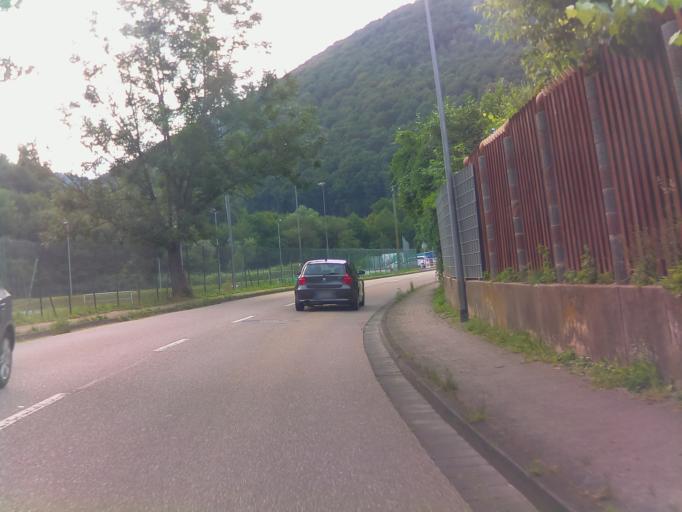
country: DE
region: Hesse
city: Neckarsteinach
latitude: 49.4108
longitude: 8.8296
